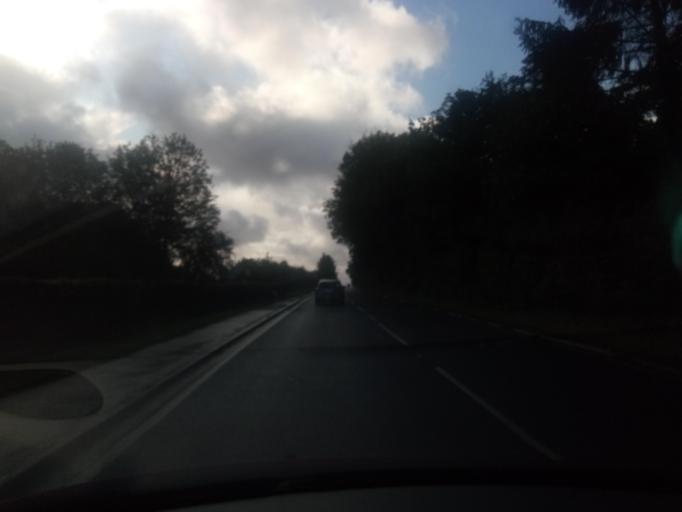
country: GB
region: England
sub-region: Cumbria
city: Carlisle
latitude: 54.9448
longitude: -2.9435
